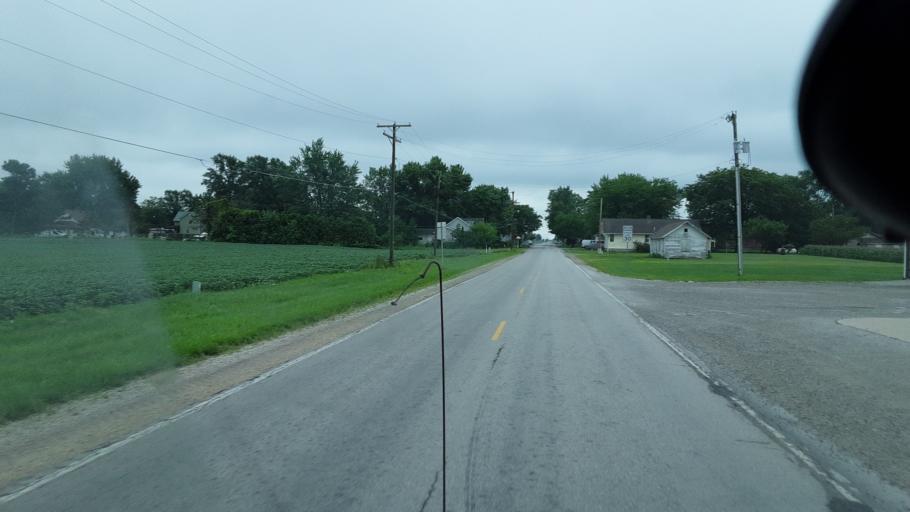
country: US
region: Indiana
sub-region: Wells County
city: Bluffton
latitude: 40.7802
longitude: -85.0908
